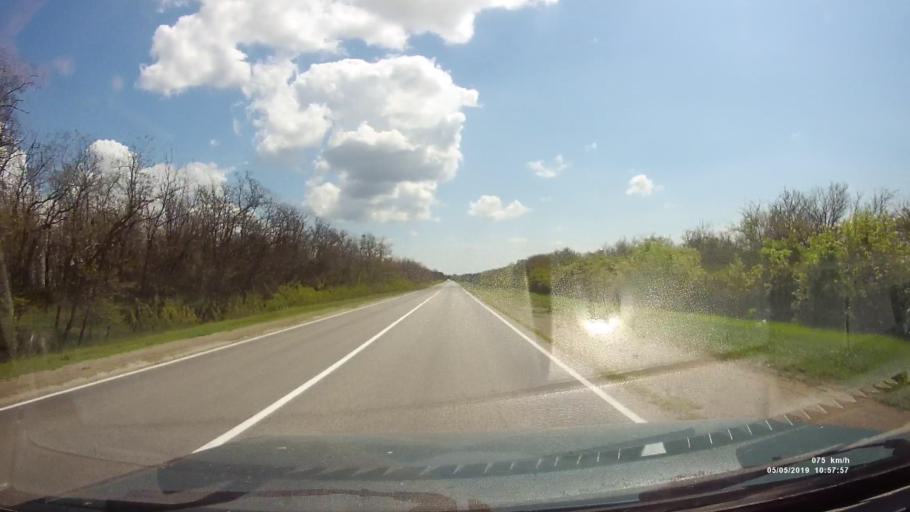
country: RU
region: Rostov
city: Ust'-Donetskiy
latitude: 47.6712
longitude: 40.8445
